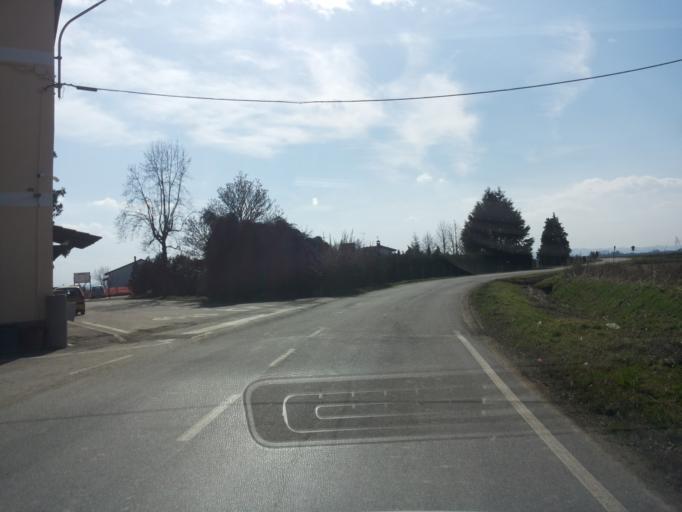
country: IT
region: Piedmont
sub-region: Provincia di Vercelli
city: Asigliano Vercellese
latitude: 45.2580
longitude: 8.4007
